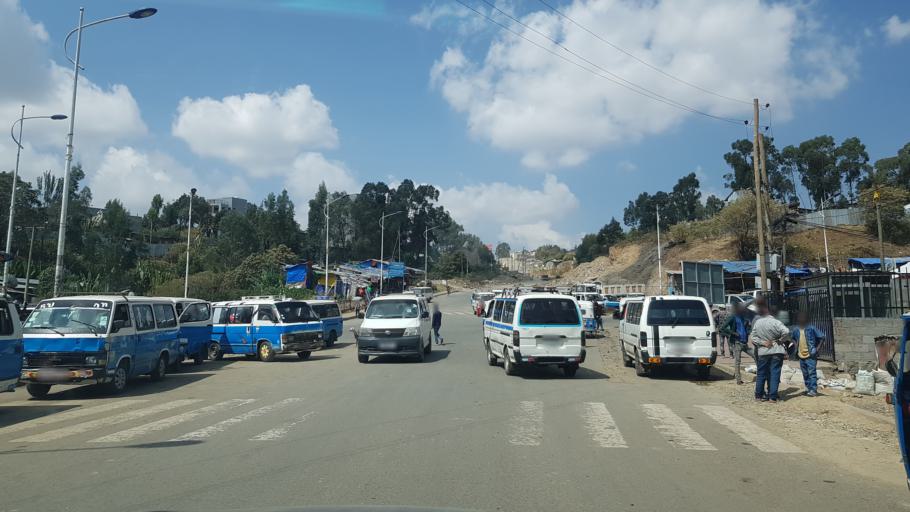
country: ET
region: Adis Abeba
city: Addis Ababa
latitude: 9.0052
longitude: 38.7073
